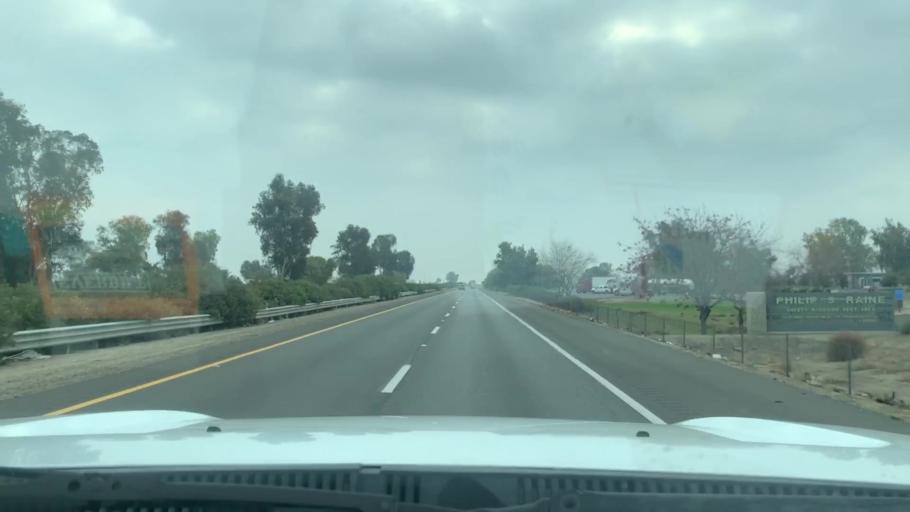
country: US
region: California
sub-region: Tulare County
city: Tipton
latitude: 36.1103
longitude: -119.3237
